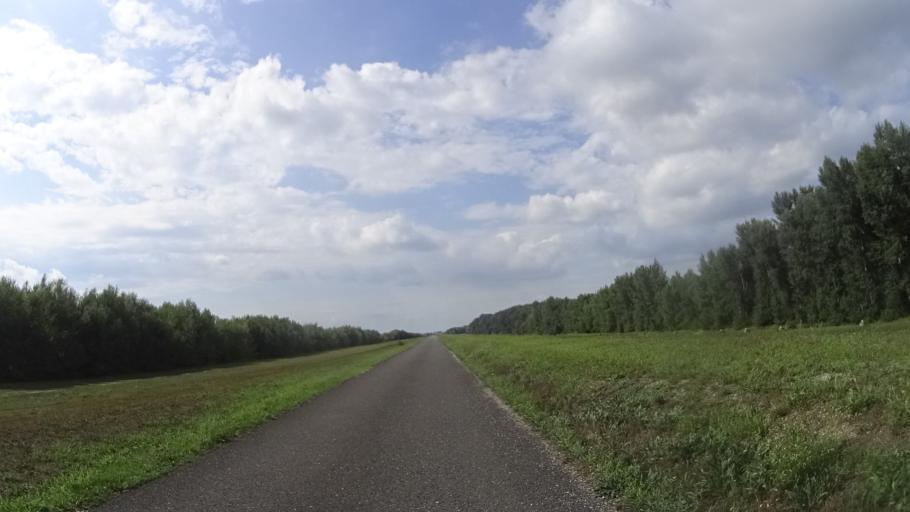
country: SK
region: Trnavsky
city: Gabcikovo
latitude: 47.8492
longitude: 17.5787
